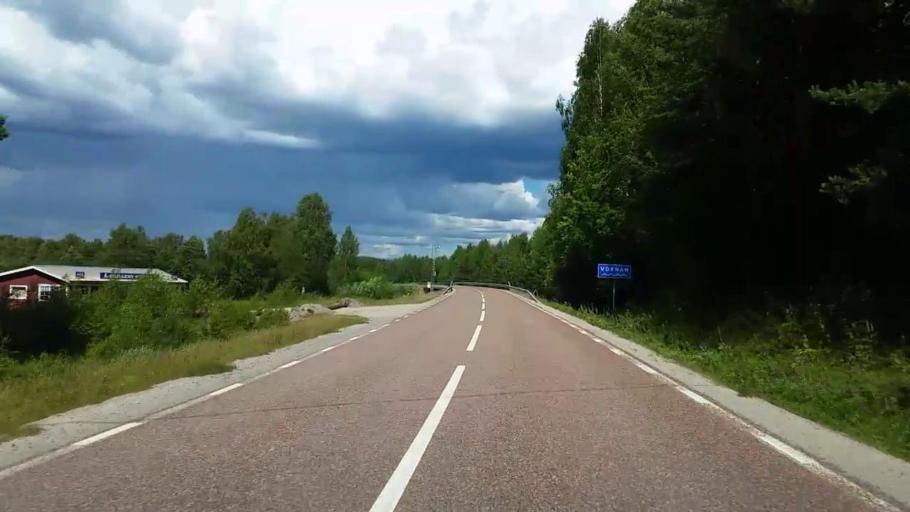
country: SE
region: Gaevleborg
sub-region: Ovanakers Kommun
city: Edsbyn
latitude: 61.3347
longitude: 15.5418
